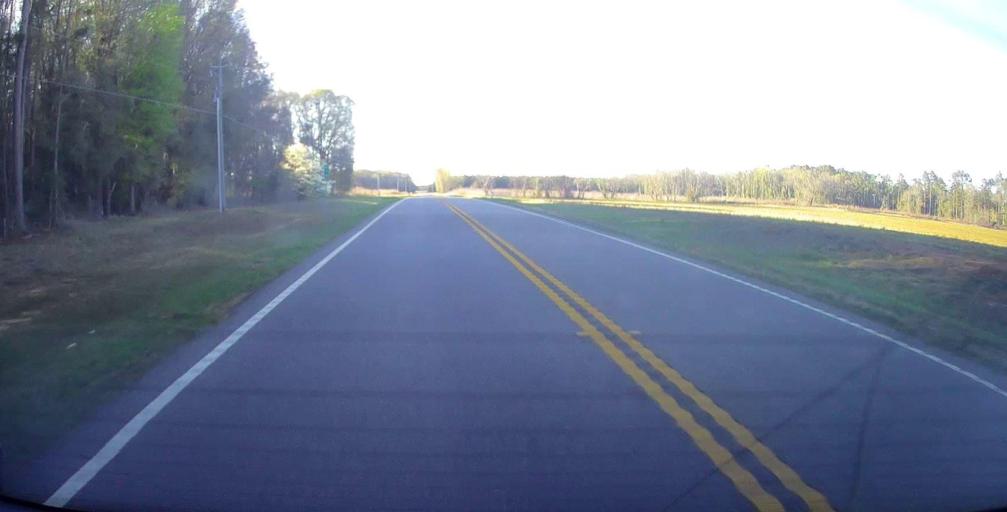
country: US
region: Georgia
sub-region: Pulaski County
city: Hawkinsville
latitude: 32.2562
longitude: -83.4148
